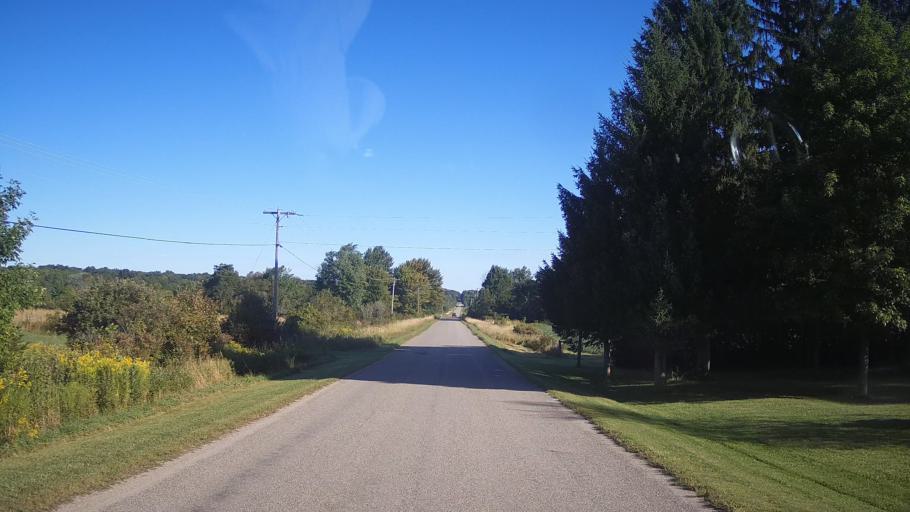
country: US
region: New York
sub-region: Jefferson County
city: Alexandria Bay
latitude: 44.4297
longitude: -75.9805
